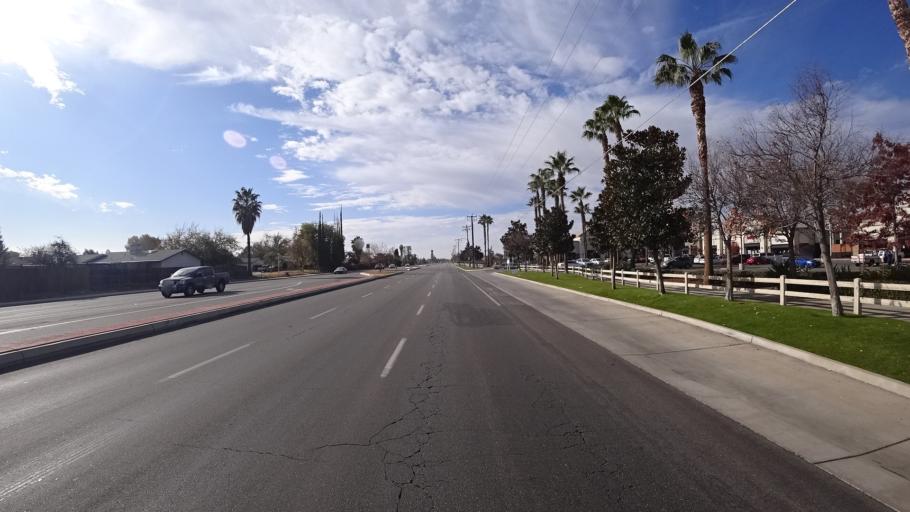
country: US
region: California
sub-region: Kern County
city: Greenacres
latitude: 35.3980
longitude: -119.1194
